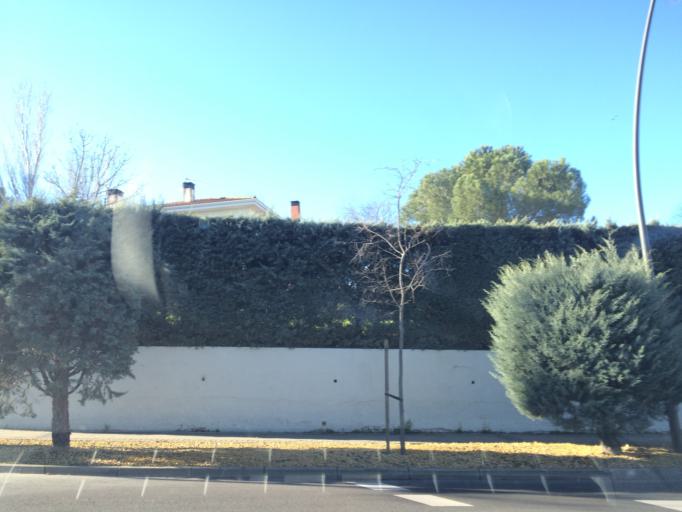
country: ES
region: Madrid
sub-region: Provincia de Madrid
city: Tres Cantos
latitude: 40.6121
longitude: -3.6896
